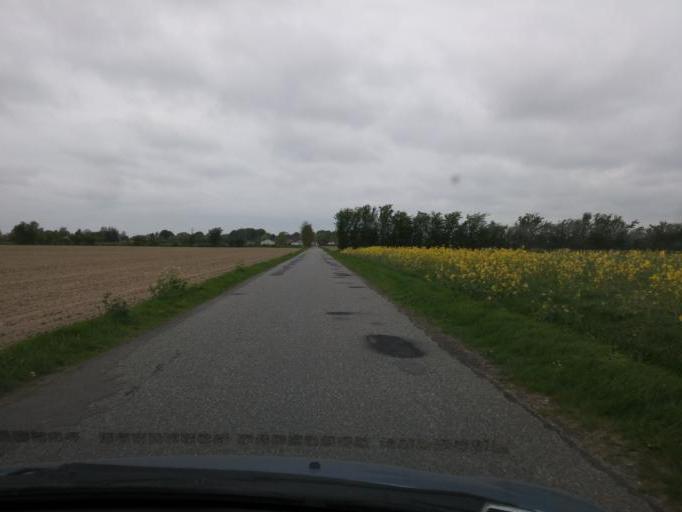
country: DK
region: South Denmark
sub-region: Odense Kommune
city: Bullerup
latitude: 55.4068
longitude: 10.5221
